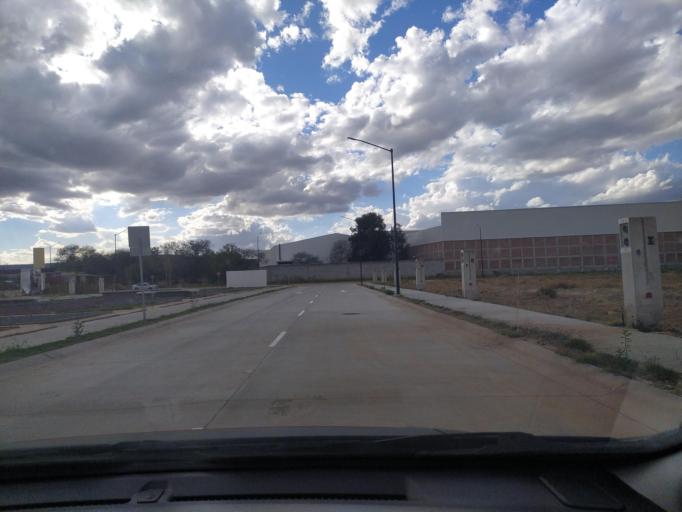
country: LA
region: Oudomxai
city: Muang La
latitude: 21.0246
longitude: 101.8239
